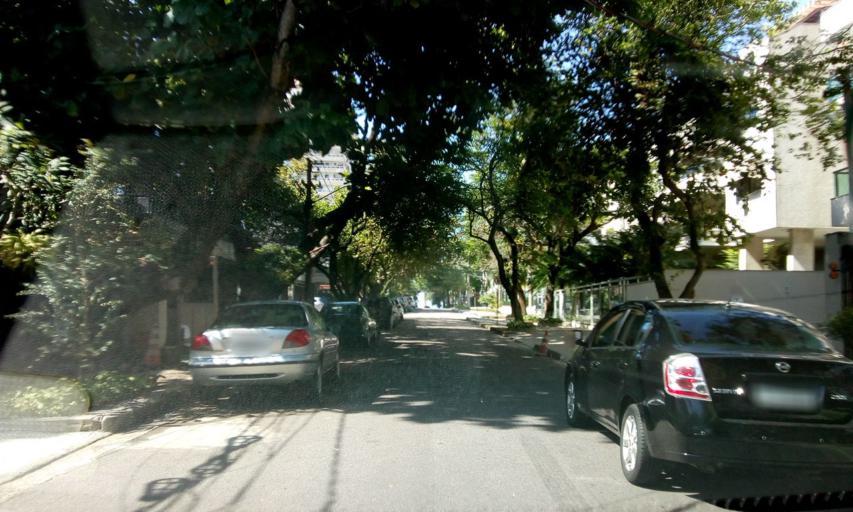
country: BR
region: Rio de Janeiro
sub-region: Rio De Janeiro
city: Rio de Janeiro
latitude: -23.0123
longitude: -43.3094
